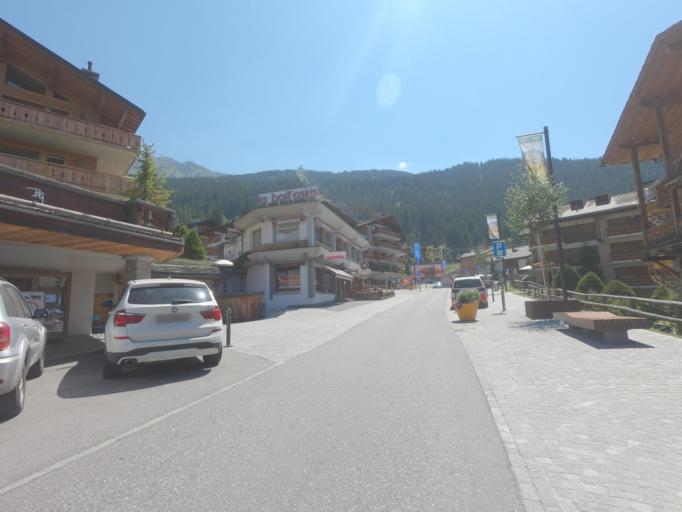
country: CH
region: Valais
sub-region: Entremont District
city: Verbier
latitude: 46.0942
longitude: 7.2319
